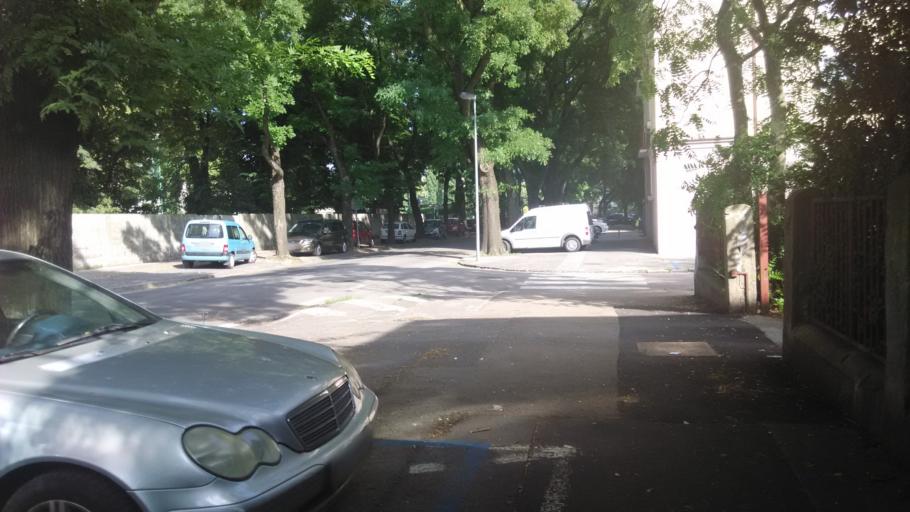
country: SK
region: Bratislavsky
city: Bratislava
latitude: 48.1619
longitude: 17.1326
